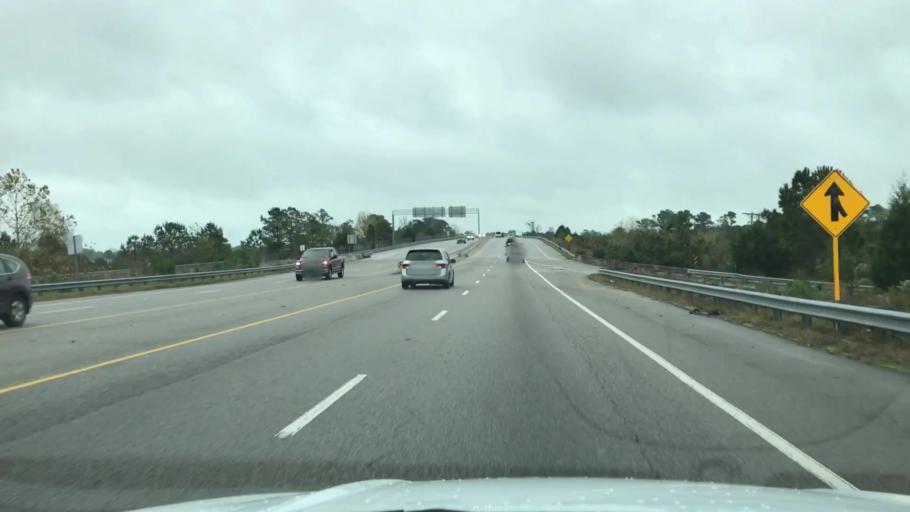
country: US
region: South Carolina
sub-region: Horry County
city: Myrtle Beach
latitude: 33.7530
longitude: -78.8519
